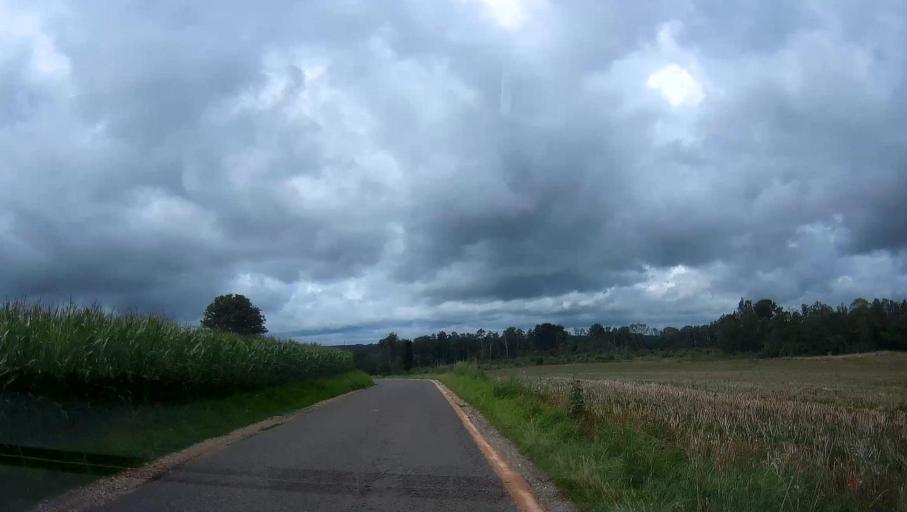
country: FR
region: Champagne-Ardenne
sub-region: Departement des Ardennes
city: Tournes
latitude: 49.7489
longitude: 4.5760
